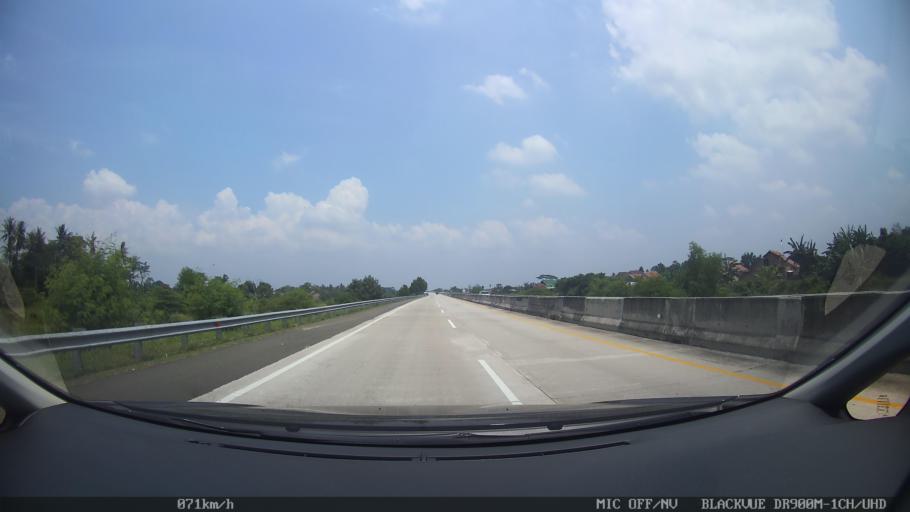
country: ID
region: Lampung
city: Kedaton
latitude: -5.3299
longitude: 105.2887
